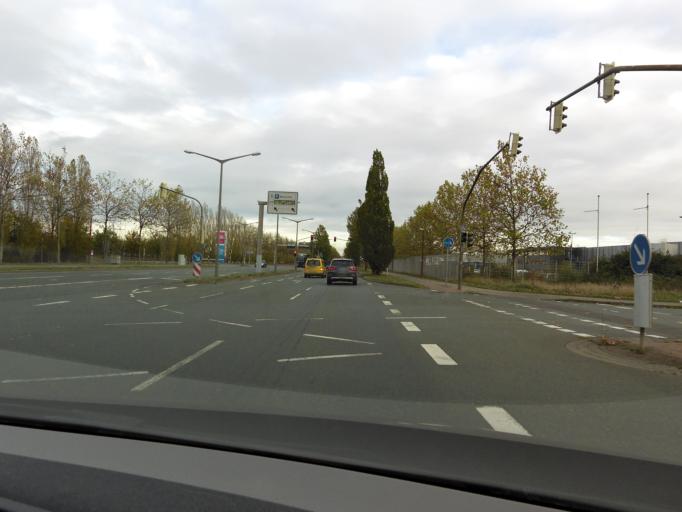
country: DE
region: Saxony
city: Rackwitz
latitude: 51.3937
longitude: 12.4049
